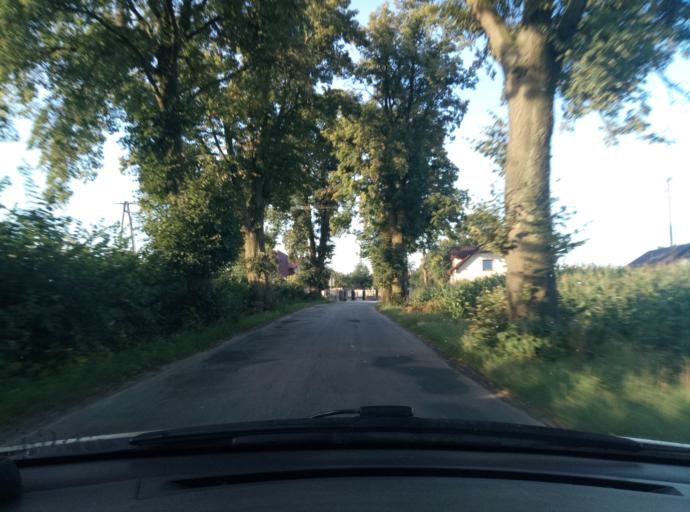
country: PL
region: Kujawsko-Pomorskie
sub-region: Powiat brodnicki
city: Jablonowo Pomorskie
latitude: 53.4113
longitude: 19.1754
